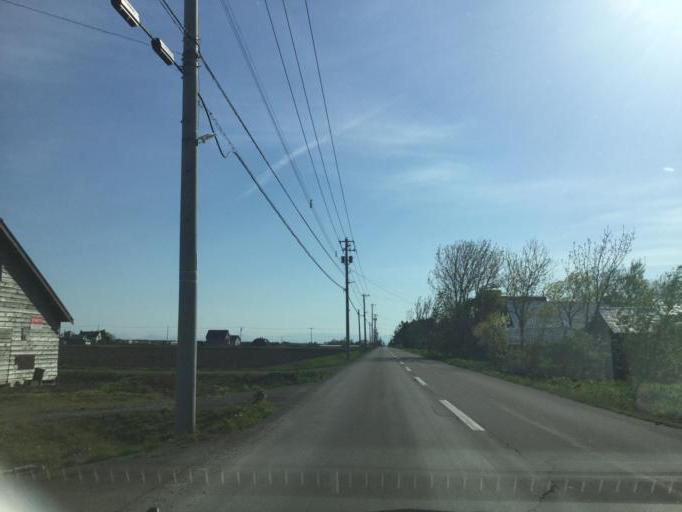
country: JP
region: Hokkaido
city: Iwamizawa
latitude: 43.1719
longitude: 141.7447
